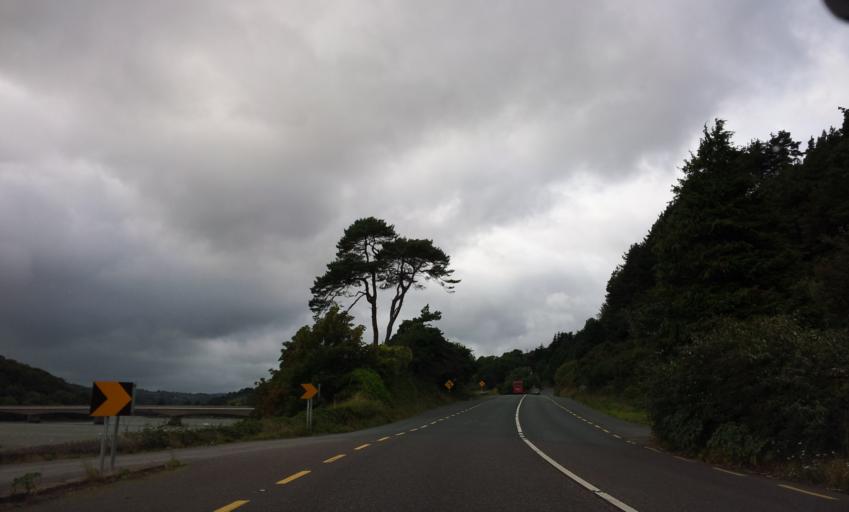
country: IE
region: Munster
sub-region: County Cork
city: Youghal
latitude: 51.9788
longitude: -7.8490
